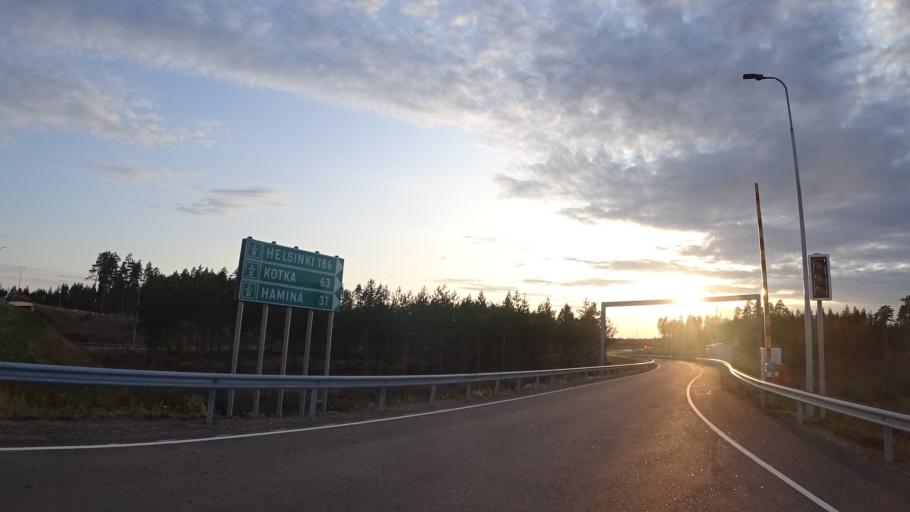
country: FI
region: Kymenlaakso
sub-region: Kotka-Hamina
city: Virojoki
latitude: 60.6112
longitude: 27.8158
